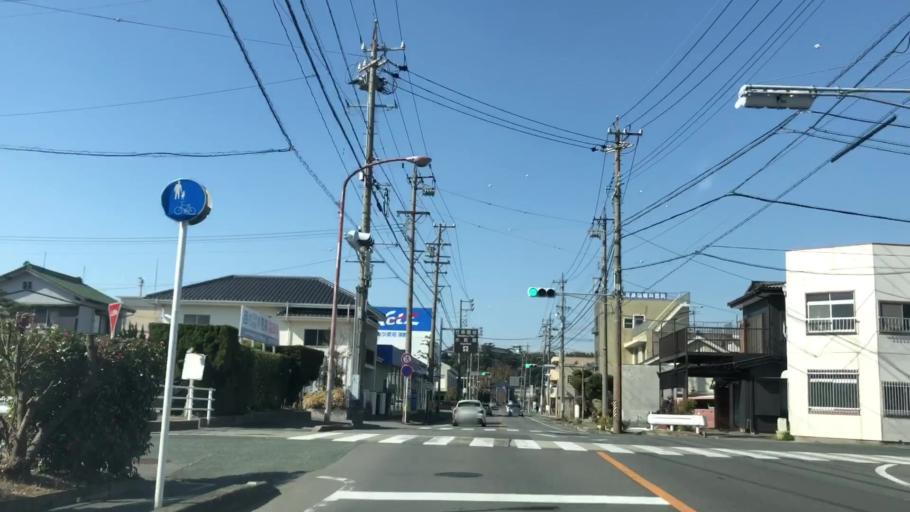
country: JP
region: Aichi
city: Gamagori
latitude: 34.8158
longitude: 137.2432
